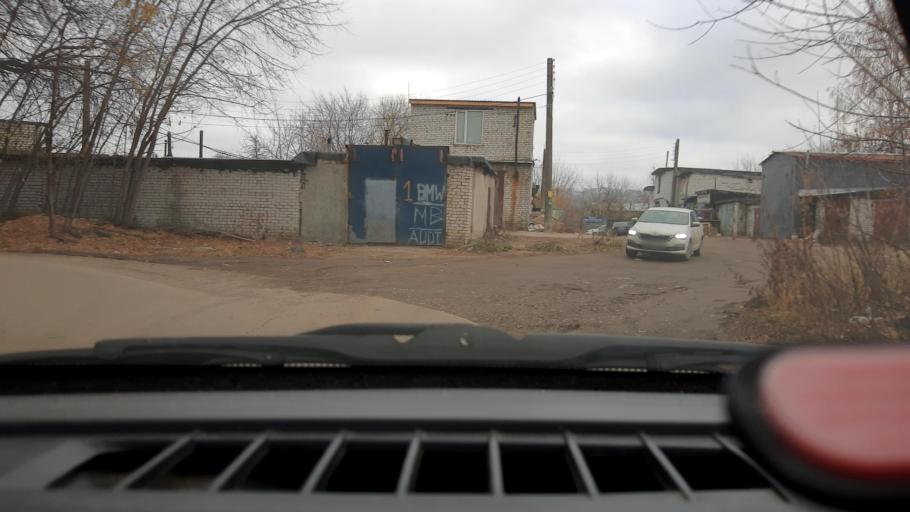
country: RU
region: Nizjnij Novgorod
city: Nizhniy Novgorod
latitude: 56.2617
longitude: 43.9446
